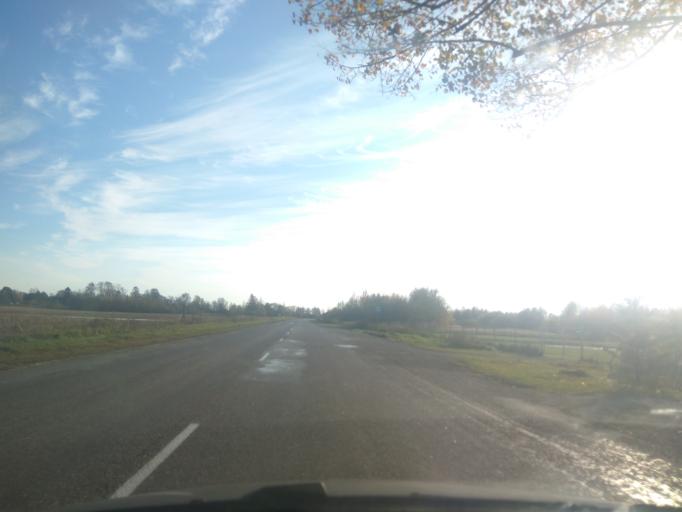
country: LV
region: Ventspils
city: Ventspils
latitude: 57.3312
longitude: 21.5639
